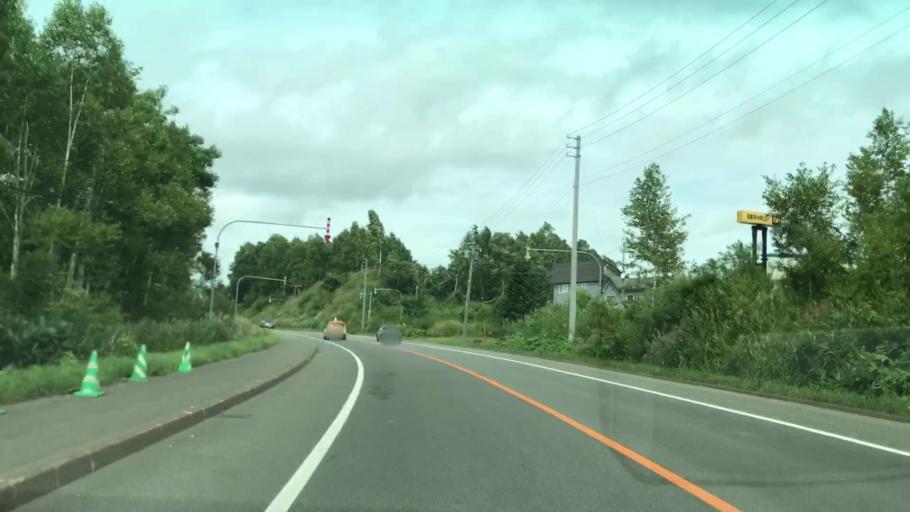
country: JP
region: Hokkaido
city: Niseko Town
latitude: 42.9119
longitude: 140.7531
